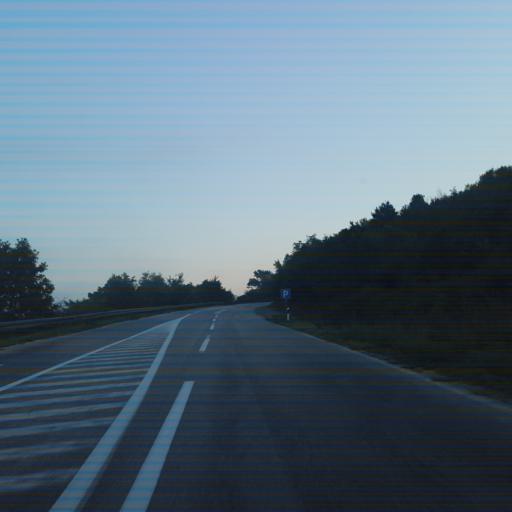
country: RS
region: Central Serbia
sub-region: Zajecarski Okrug
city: Zajecar
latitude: 43.9842
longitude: 22.2952
